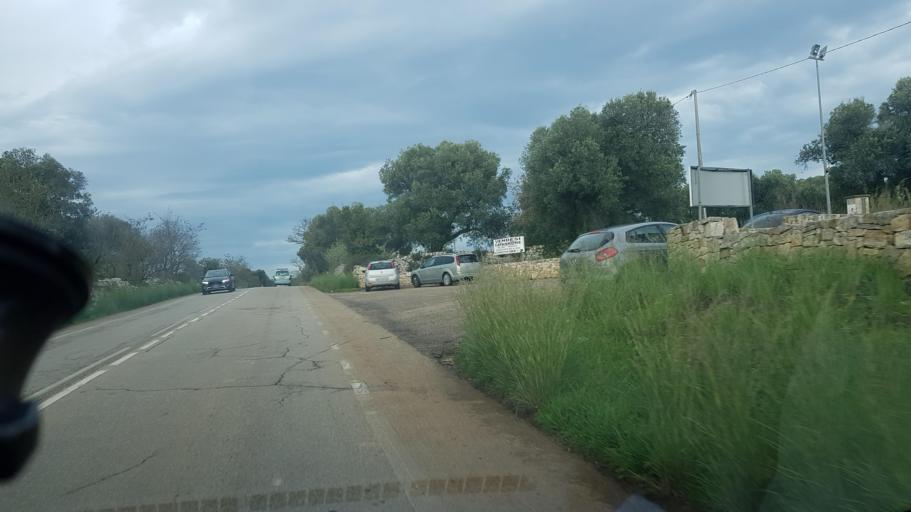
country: IT
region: Apulia
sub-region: Provincia di Brindisi
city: Carovigno
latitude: 40.6858
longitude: 17.6786
